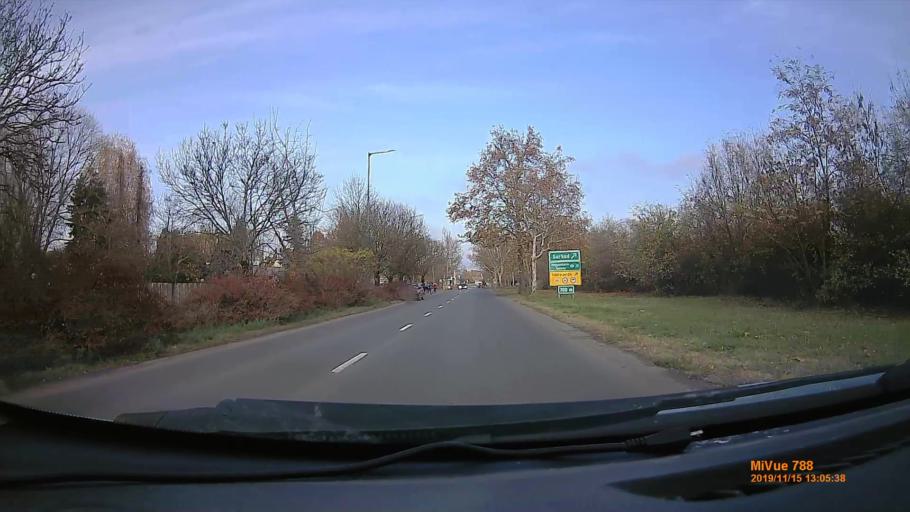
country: HU
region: Bekes
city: Gyula
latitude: 46.6375
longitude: 21.2615
